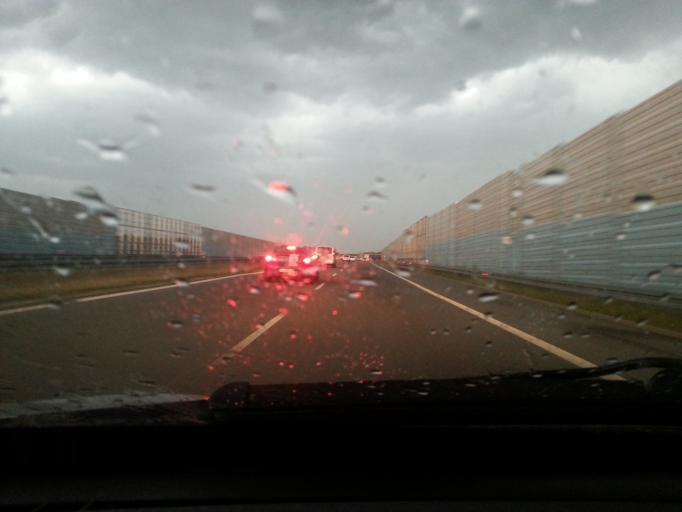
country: PL
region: Lodz Voivodeship
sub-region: powiat Lowicki
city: Lyszkowice
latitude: 51.9693
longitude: 19.8664
